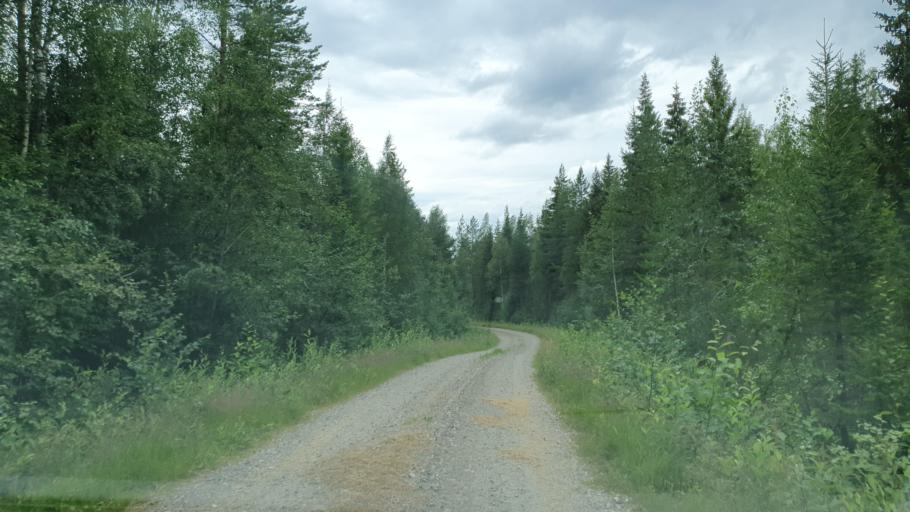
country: FI
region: Kainuu
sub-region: Kehys-Kainuu
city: Kuhmo
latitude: 64.2030
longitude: 29.4013
